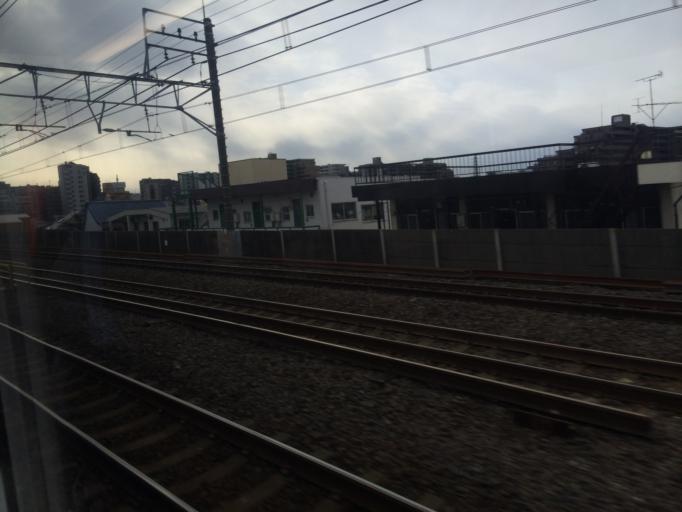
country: JP
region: Tokyo
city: Urayasu
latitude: 35.7234
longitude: 139.9216
